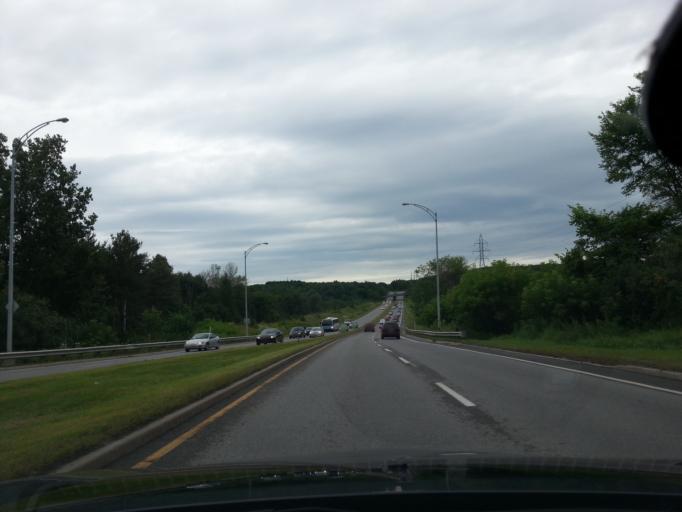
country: CA
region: Quebec
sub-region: Outaouais
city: Gatineau
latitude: 45.4462
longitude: -75.7526
